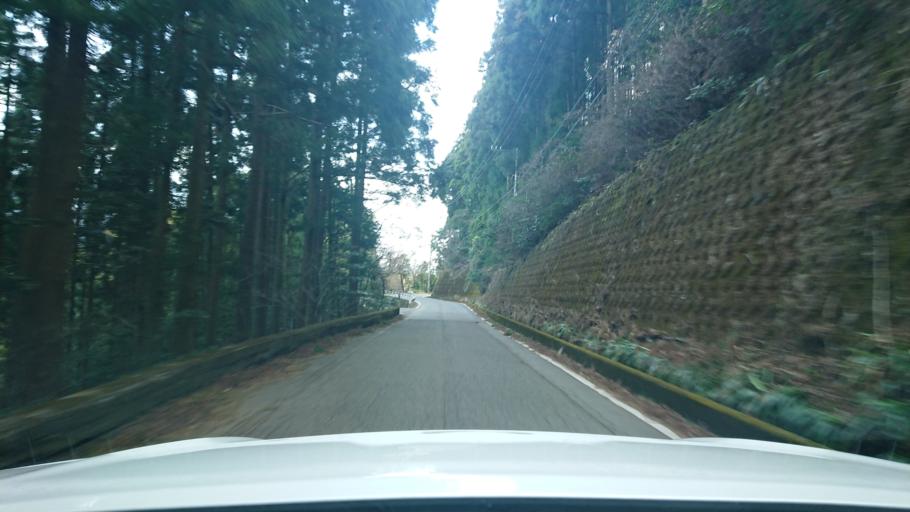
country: JP
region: Tokushima
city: Ishii
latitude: 33.9137
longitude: 134.4036
